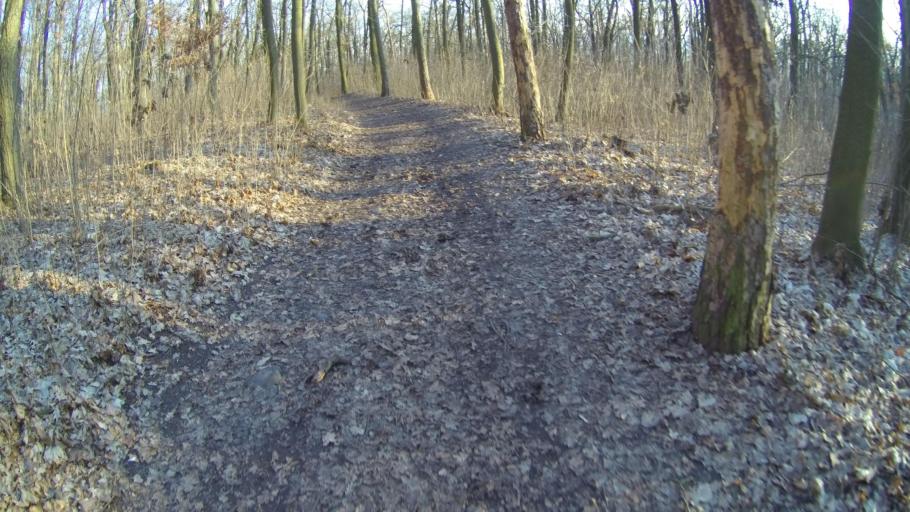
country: CZ
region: Ustecky
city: Roudnice nad Labem
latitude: 50.3830
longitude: 14.2856
